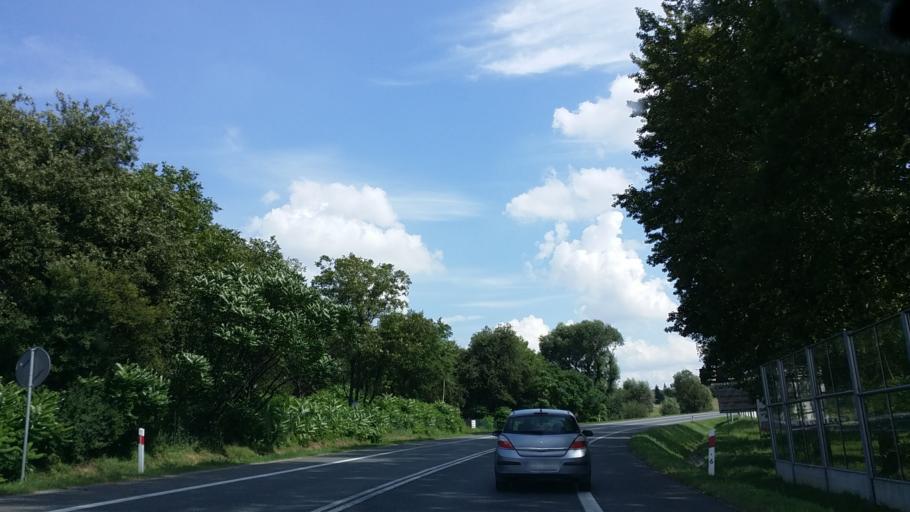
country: PL
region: Lesser Poland Voivodeship
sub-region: Powiat wielicki
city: Wieliczka
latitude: 49.9938
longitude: 20.0776
